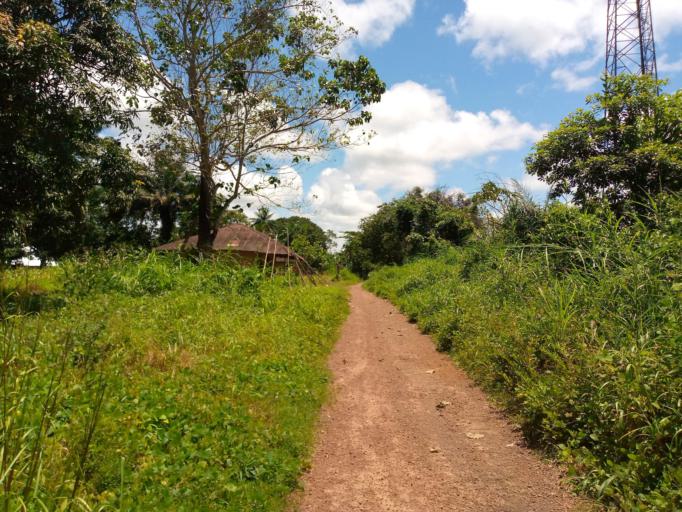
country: SL
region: Northern Province
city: Makeni
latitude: 9.0322
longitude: -12.1628
